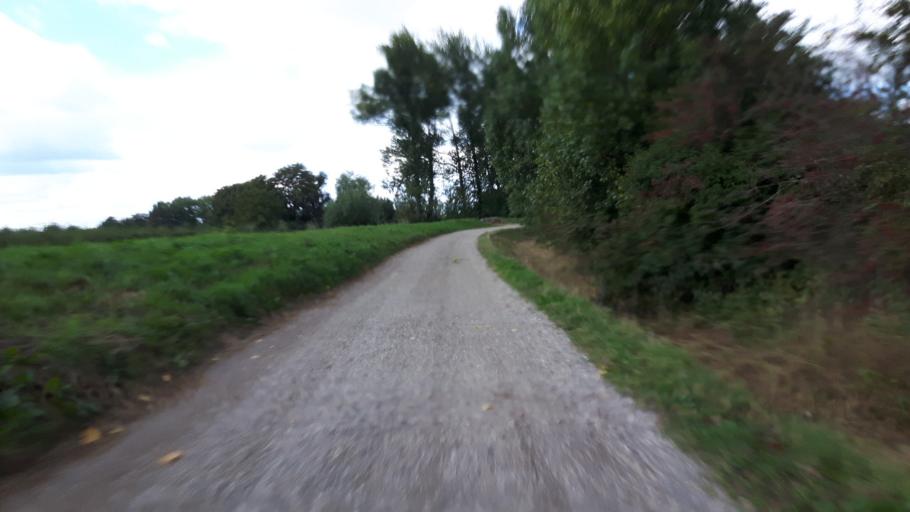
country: NL
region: South Holland
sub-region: Gemeente Leerdam
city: Leerdam
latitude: 51.8720
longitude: 5.1242
